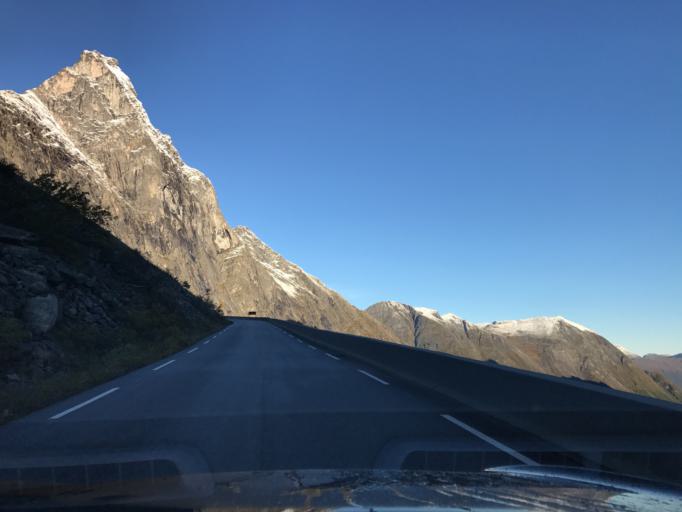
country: NO
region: More og Romsdal
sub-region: Rauma
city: Andalsnes
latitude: 62.4615
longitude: 7.6665
